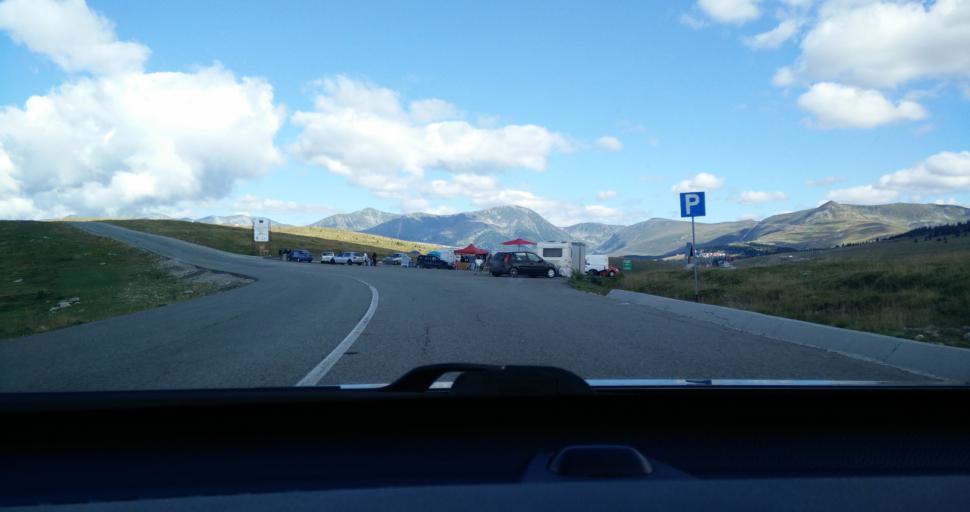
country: RO
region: Gorj
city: Novaci-Straini
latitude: 45.2593
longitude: 23.6948
